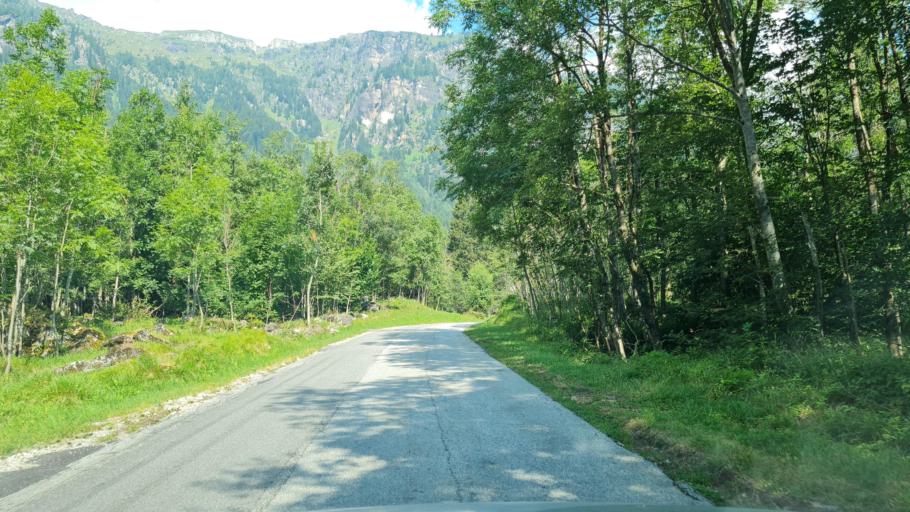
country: IT
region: Piedmont
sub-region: Provincia Verbano-Cusio-Ossola
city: Baceno
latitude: 46.2909
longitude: 8.2699
